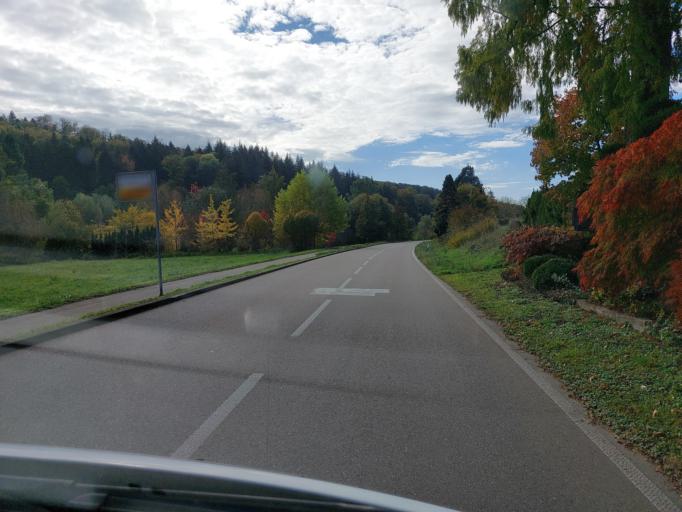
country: DE
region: Baden-Wuerttemberg
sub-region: Freiburg Region
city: Malterdingen
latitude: 48.1592
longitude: 7.8287
